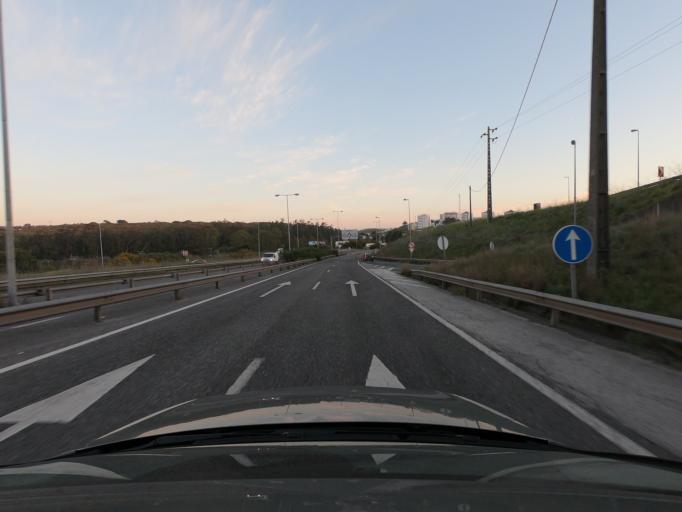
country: PT
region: Lisbon
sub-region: Sintra
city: Queluz
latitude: 38.7490
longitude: -9.2642
